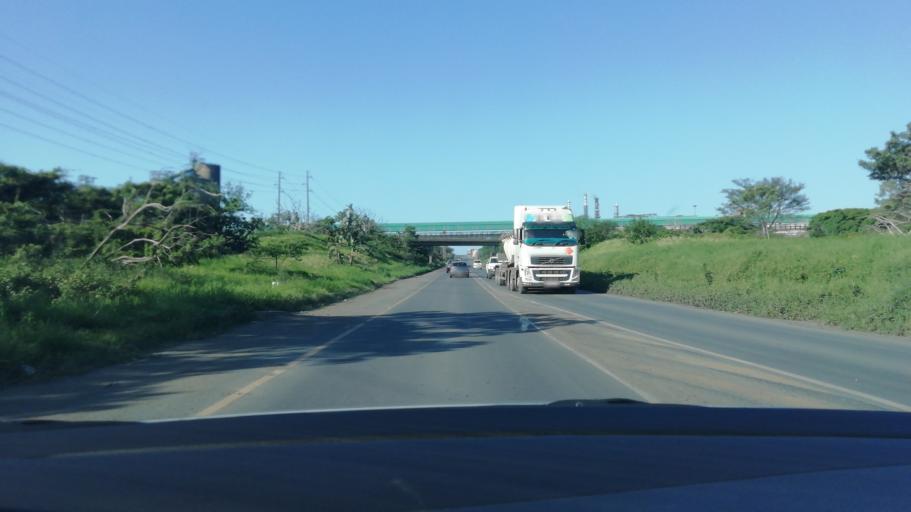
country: ZA
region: KwaZulu-Natal
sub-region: uThungulu District Municipality
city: Richards Bay
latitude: -28.7802
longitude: 32.0289
